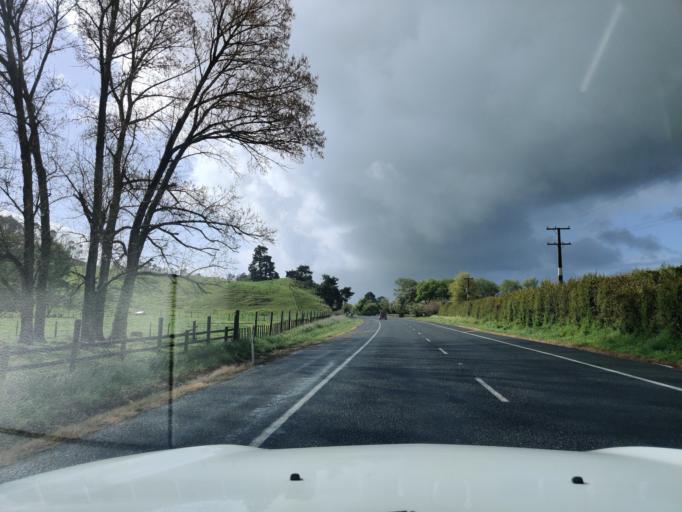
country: NZ
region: Waikato
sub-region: Waipa District
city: Cambridge
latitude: -37.9218
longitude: 175.5607
